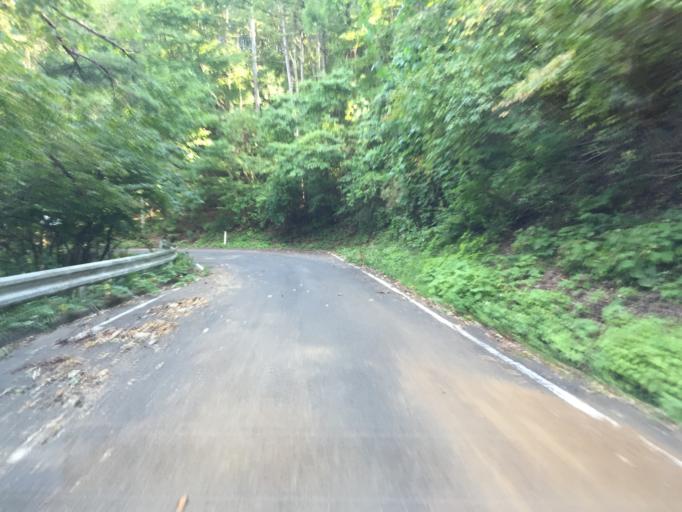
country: JP
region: Fukushima
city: Yanagawamachi-saiwaicho
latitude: 37.8451
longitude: 140.6924
